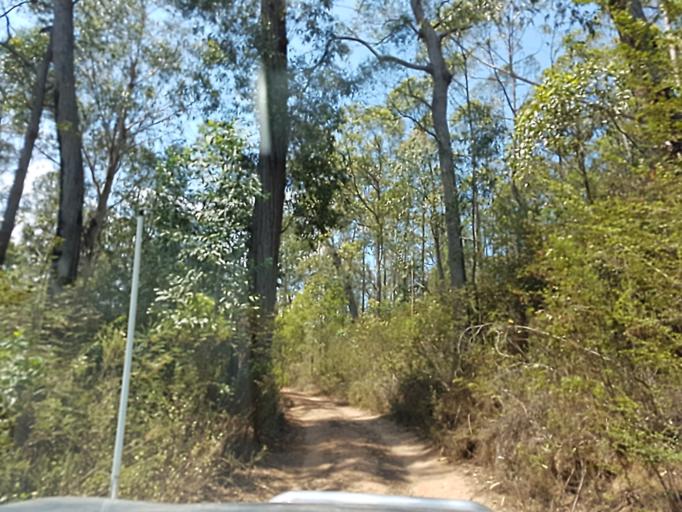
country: AU
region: Victoria
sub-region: East Gippsland
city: Lakes Entrance
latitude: -37.4040
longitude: 148.3165
